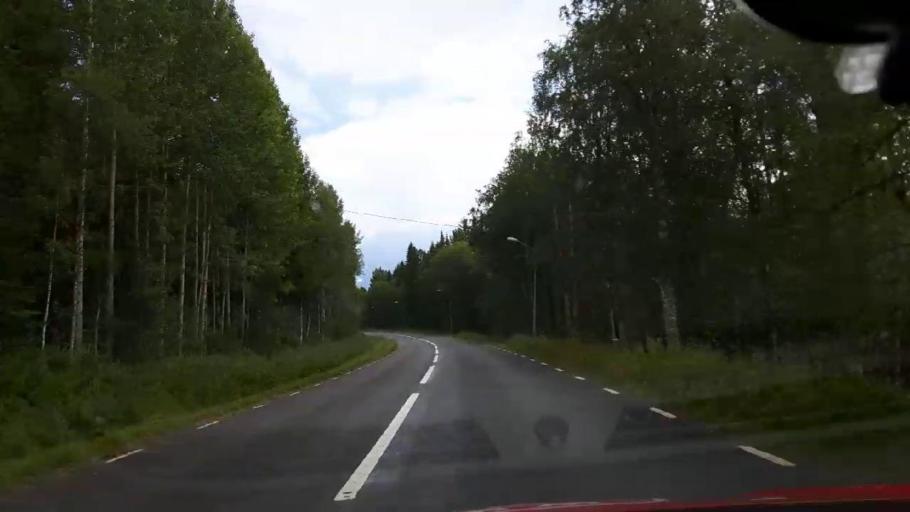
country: SE
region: Jaemtland
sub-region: Stroemsunds Kommun
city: Stroemsund
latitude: 64.3377
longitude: 14.9564
